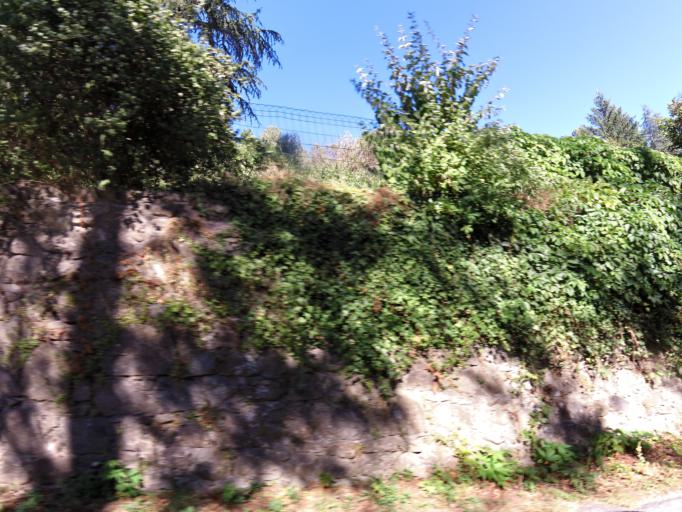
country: FR
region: Languedoc-Roussillon
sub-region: Departement du Gard
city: Saint-Jean-du-Gard
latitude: 44.1131
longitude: 3.8729
